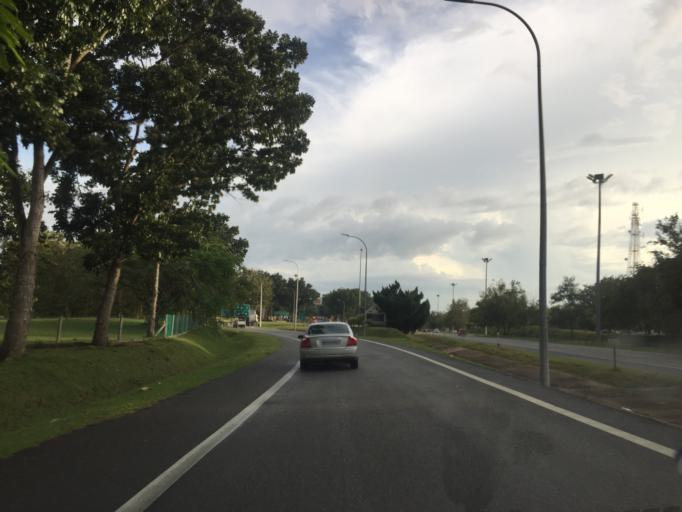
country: MY
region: Kedah
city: Gurun
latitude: 5.8342
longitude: 100.4878
